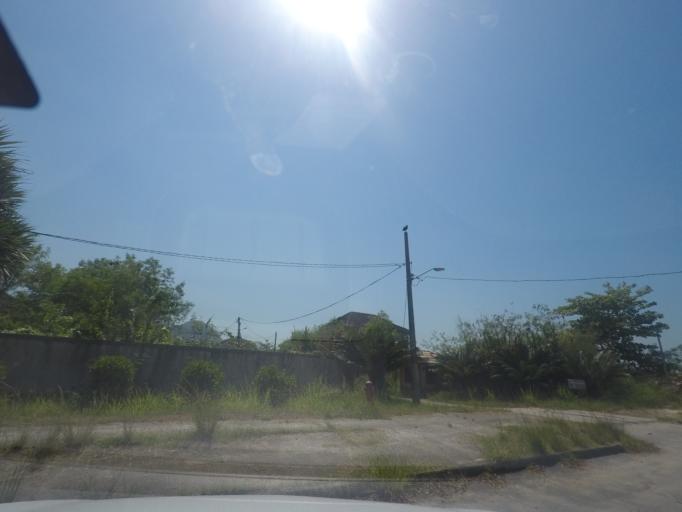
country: BR
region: Rio de Janeiro
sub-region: Nilopolis
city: Nilopolis
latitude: -22.9917
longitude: -43.4795
